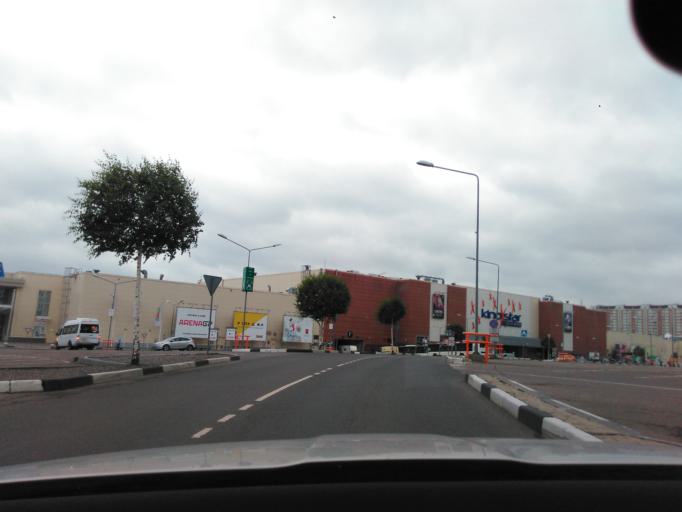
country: RU
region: Moscow
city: Khimki
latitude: 55.9109
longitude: 37.3921
